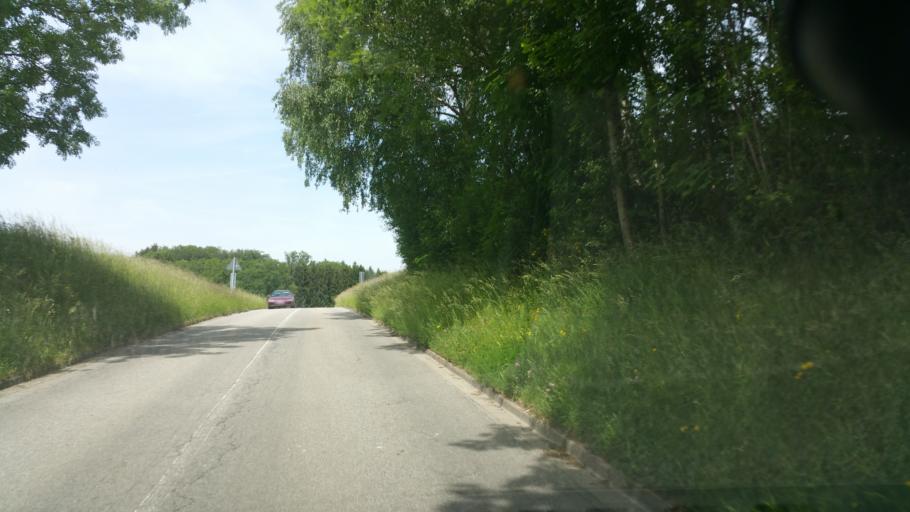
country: DE
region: Bavaria
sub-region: Upper Bavaria
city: Aschau im Chiemgau
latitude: 47.7976
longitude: 12.3247
